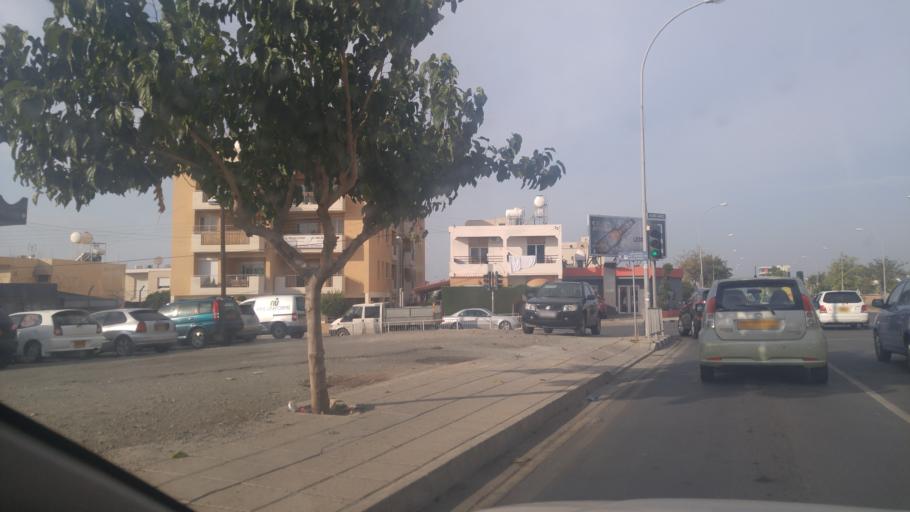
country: CY
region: Limassol
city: Limassol
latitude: 34.6979
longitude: 33.0404
